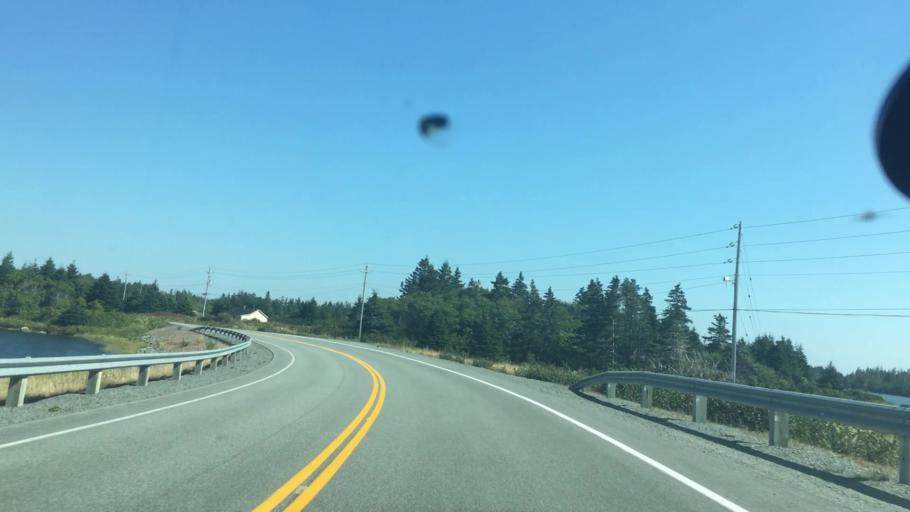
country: CA
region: Nova Scotia
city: New Glasgow
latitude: 44.9181
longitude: -62.3063
